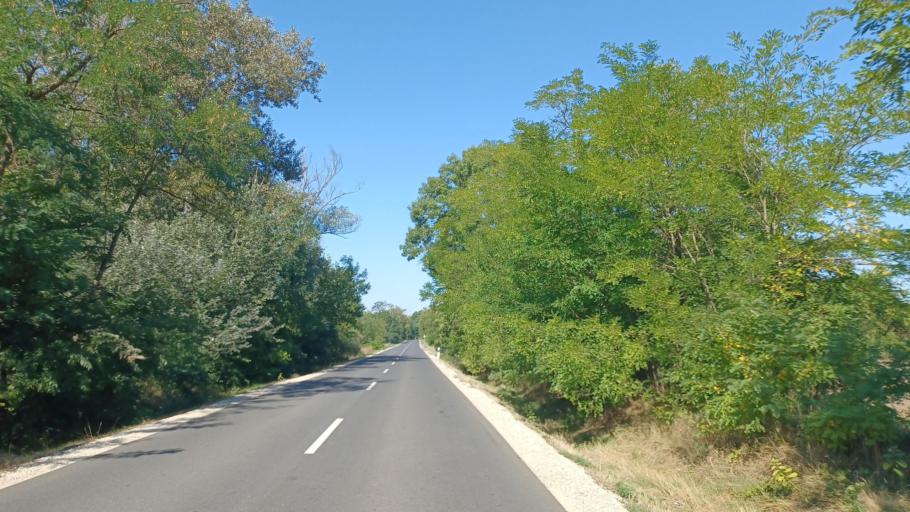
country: HU
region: Tolna
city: Nemetker
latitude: 46.7375
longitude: 18.7116
